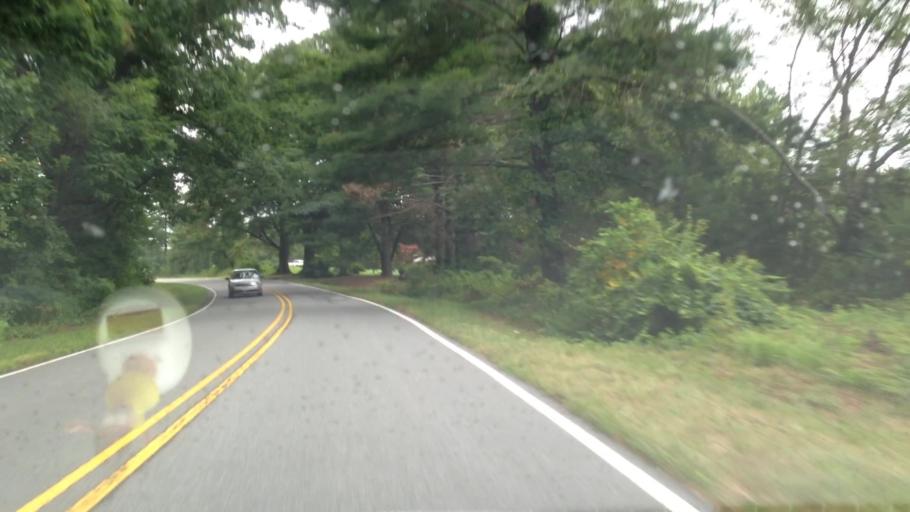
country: US
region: North Carolina
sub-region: Rockingham County
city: Mayodan
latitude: 36.4033
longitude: -80.0420
